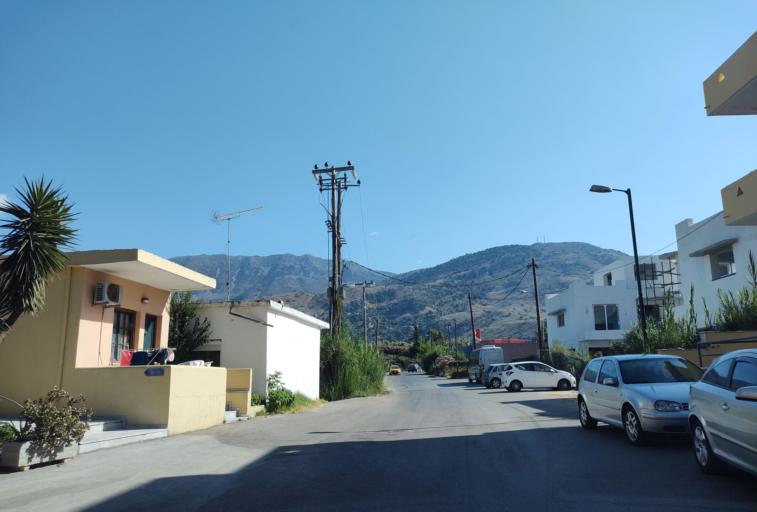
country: GR
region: Crete
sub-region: Nomos Chanias
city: Georgioupolis
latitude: 35.3594
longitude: 24.2624
